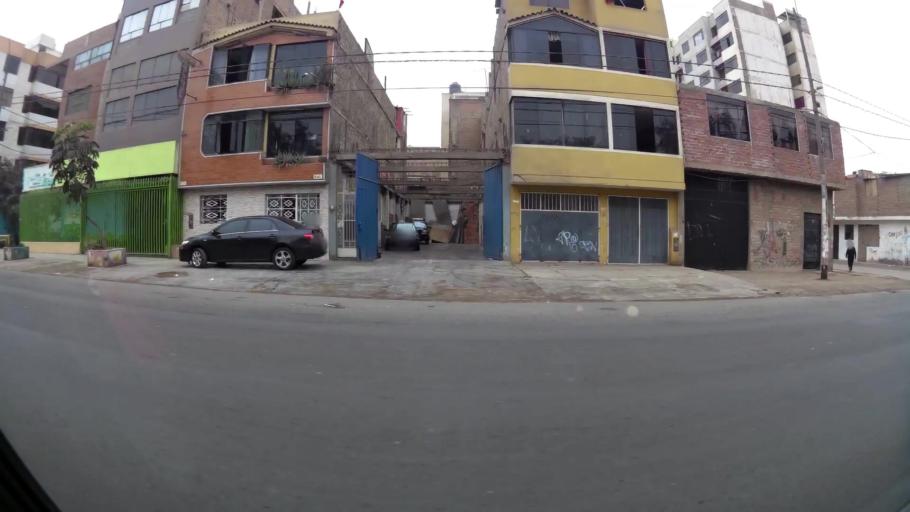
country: PE
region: Lima
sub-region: Lima
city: Independencia
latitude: -11.9552
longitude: -77.0753
